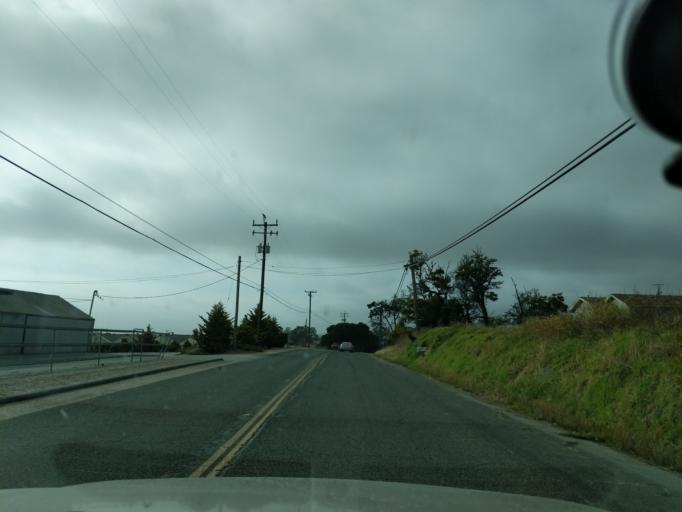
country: US
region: California
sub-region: Monterey County
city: Elkhorn
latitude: 36.8007
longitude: -121.7216
